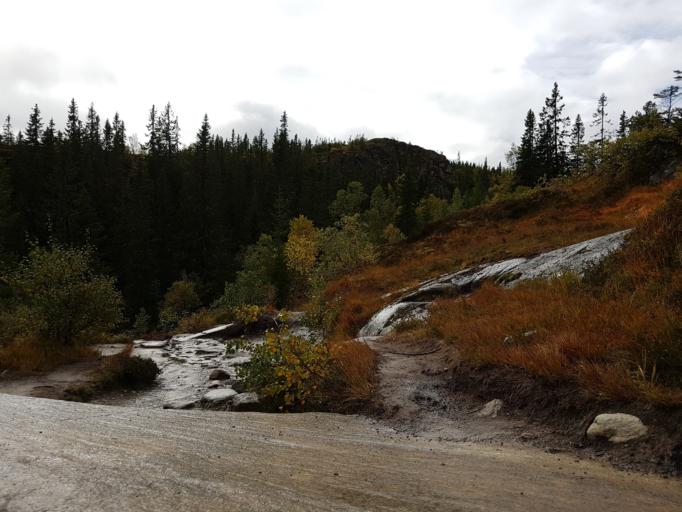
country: NO
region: Sor-Trondelag
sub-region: Melhus
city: Melhus
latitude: 63.4071
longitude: 10.2054
